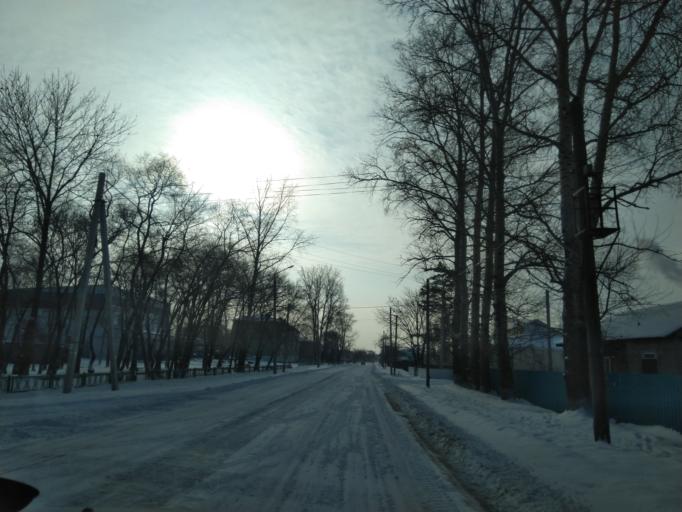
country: RU
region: Amur
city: Poyarkovo
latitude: 49.6254
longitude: 128.6505
